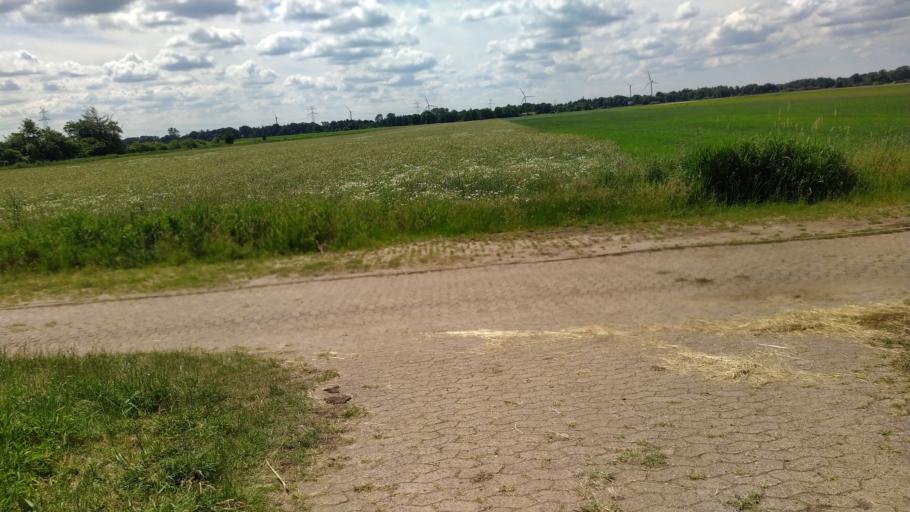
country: DE
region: Lower Saxony
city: Estorf
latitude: 53.5662
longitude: 9.1715
